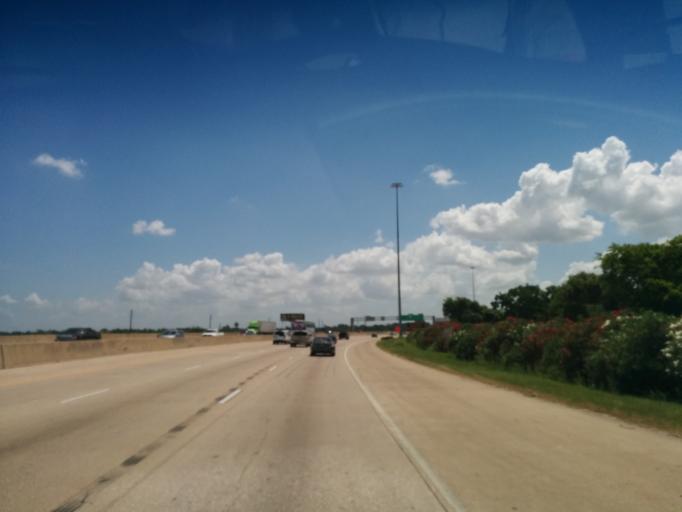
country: US
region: Texas
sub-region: Harris County
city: Highlands
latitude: 29.7948
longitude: -95.0724
